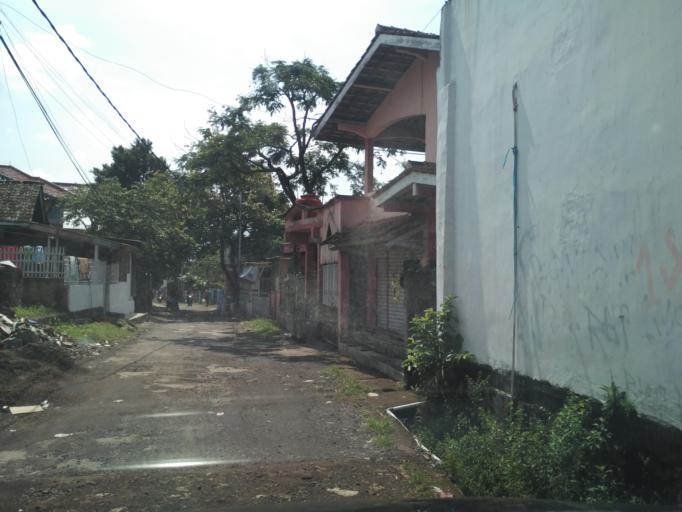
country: ID
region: West Java
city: Ciranjang-hilir
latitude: -6.8044
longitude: 107.1146
